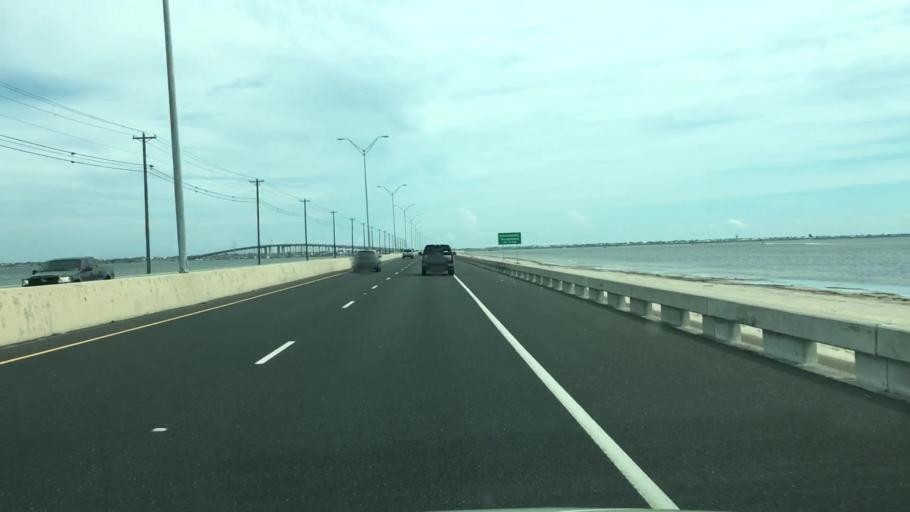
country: US
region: Texas
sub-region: Nueces County
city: Corpus Christi
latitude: 27.6471
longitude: -97.2516
